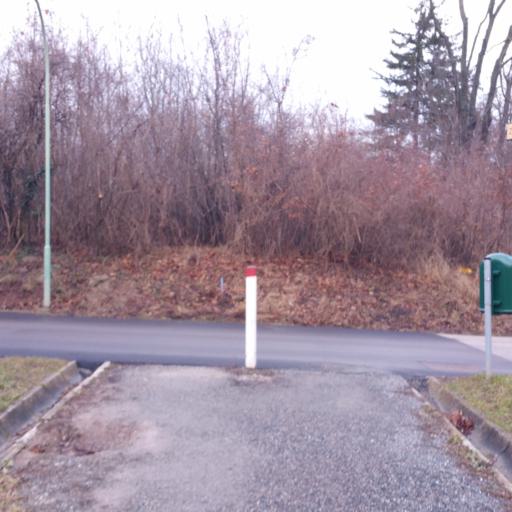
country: AT
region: Vienna
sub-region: Wien Stadt
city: Vienna
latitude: 48.2108
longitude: 16.2821
